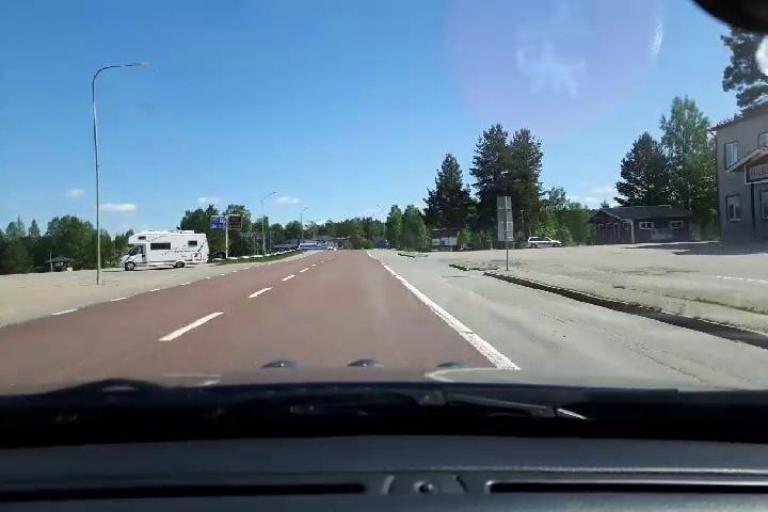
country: SE
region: Jaemtland
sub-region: Harjedalens Kommun
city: Sveg
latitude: 62.1738
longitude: 14.9420
